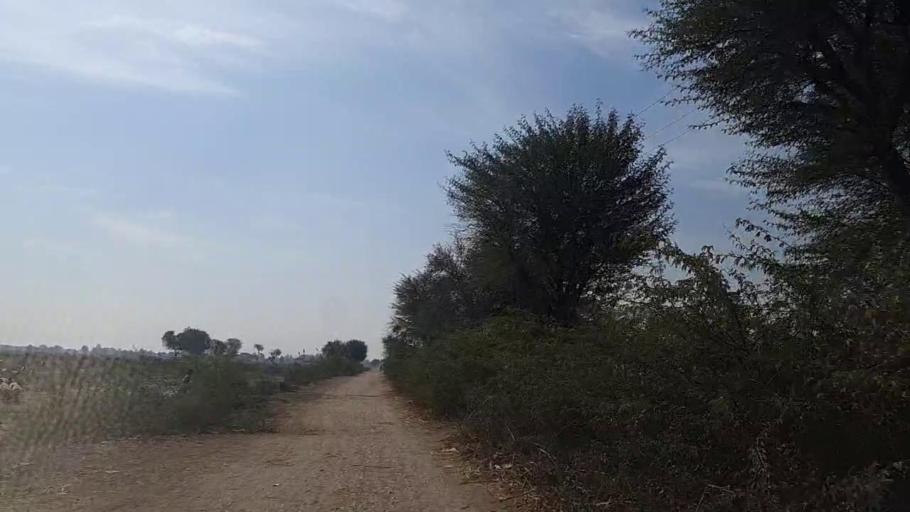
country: PK
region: Sindh
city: Mirpur Khas
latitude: 25.4810
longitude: 68.9745
